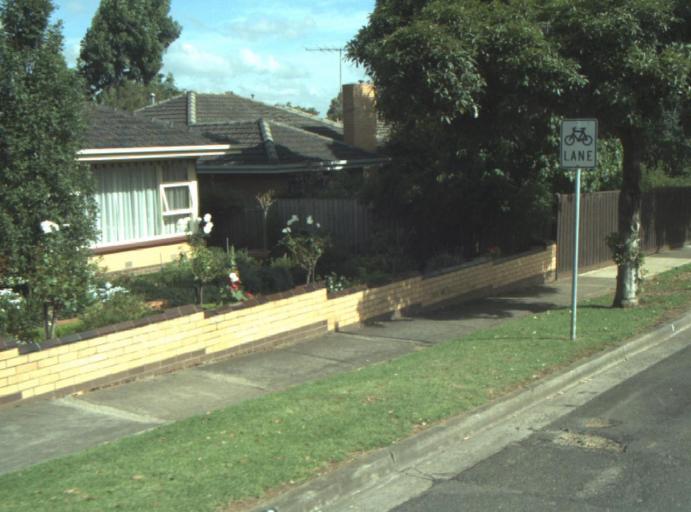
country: AU
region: Victoria
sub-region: Greater Geelong
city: Wandana Heights
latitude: -38.1728
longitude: 144.3303
